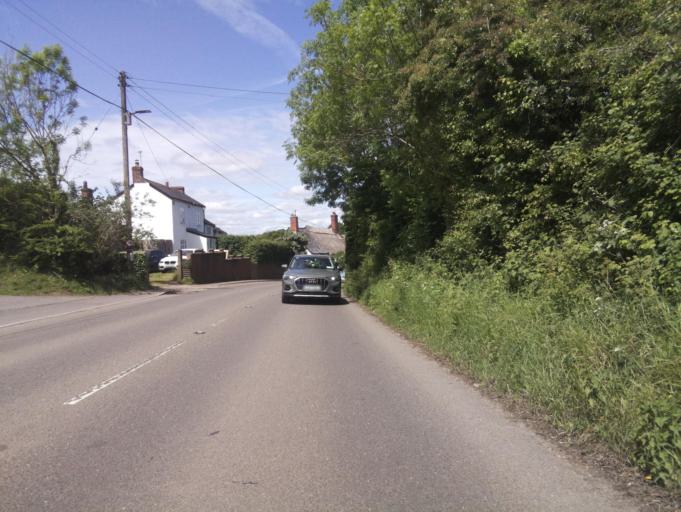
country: GB
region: England
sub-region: Devon
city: Uffculme
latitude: 50.8449
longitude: -3.3214
